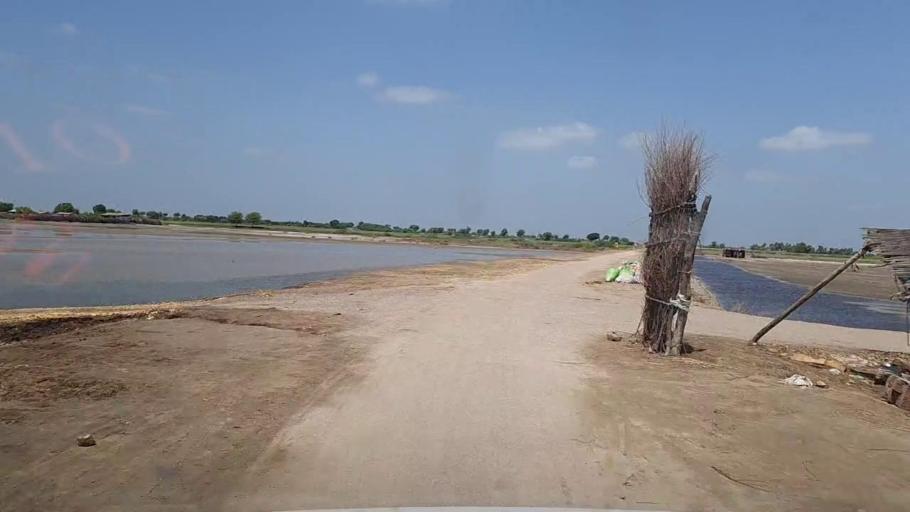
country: PK
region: Sindh
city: Kario
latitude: 24.6964
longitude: 68.5861
